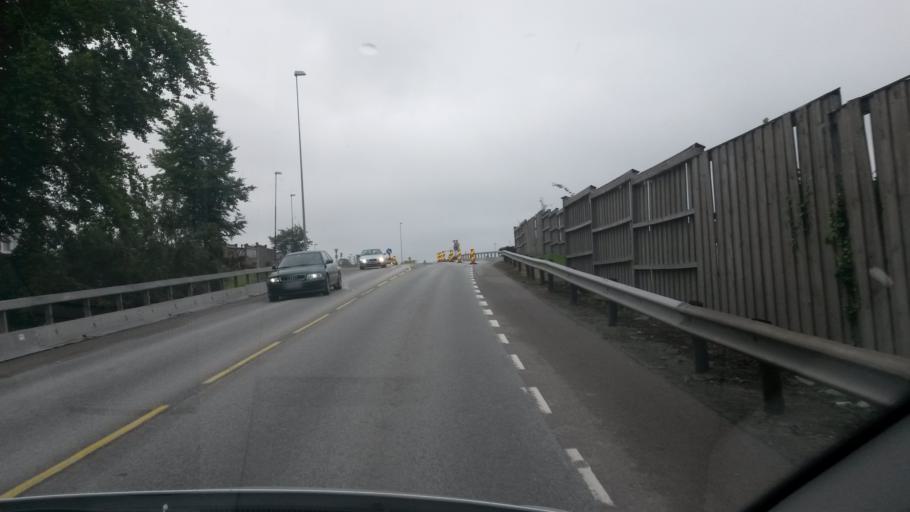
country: NO
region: Rogaland
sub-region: Sandnes
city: Sandnes
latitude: 58.8359
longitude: 5.7216
